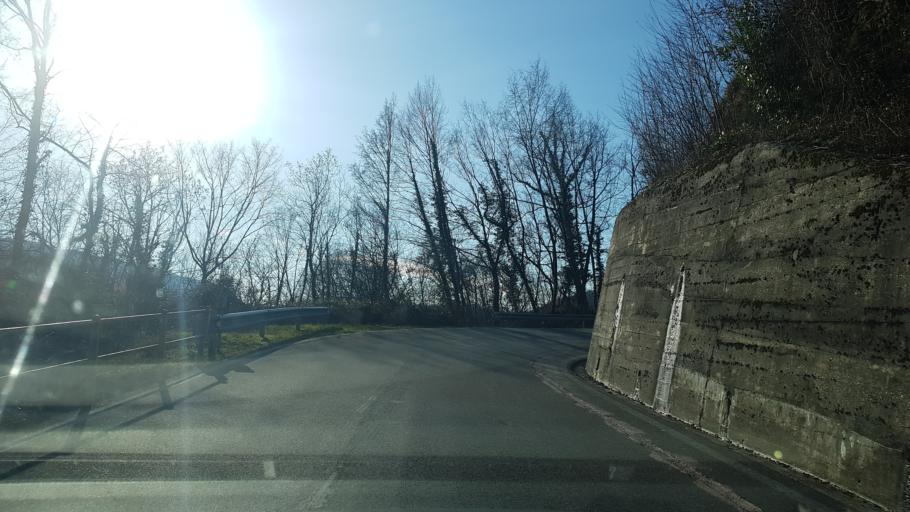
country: IT
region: Friuli Venezia Giulia
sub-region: Provincia di Udine
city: Forgaria nel Friuli
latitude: 46.2226
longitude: 12.9921
